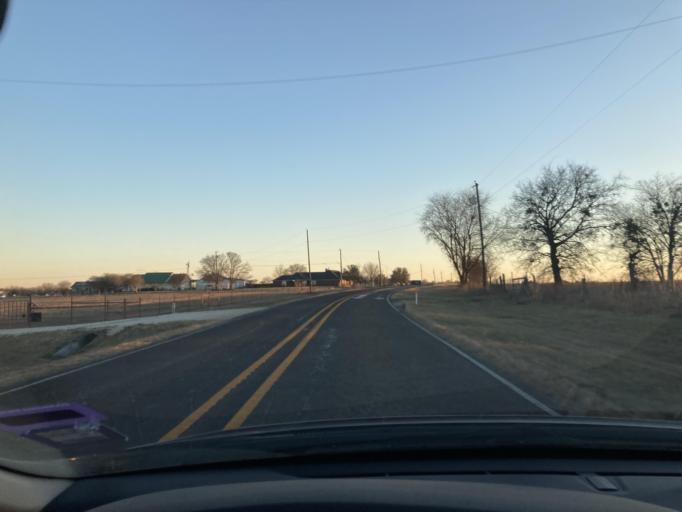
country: US
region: Texas
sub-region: Ellis County
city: Waxahachie
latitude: 32.3379
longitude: -96.8738
